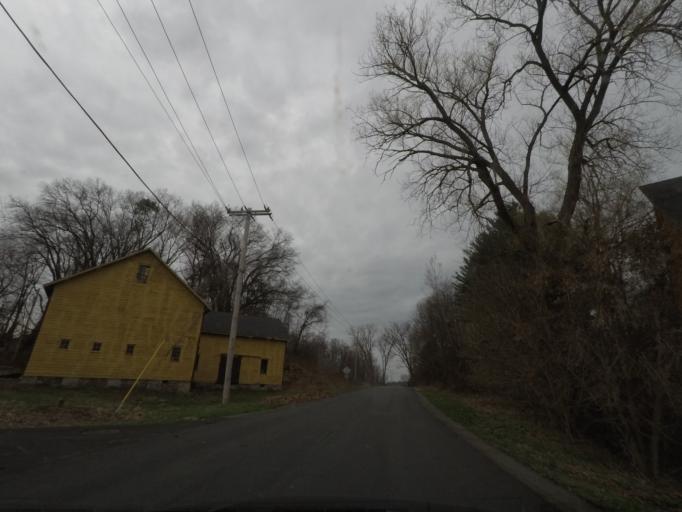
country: US
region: New York
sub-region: Rensselaer County
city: Castleton-on-Hudson
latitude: 42.5559
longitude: -73.7834
